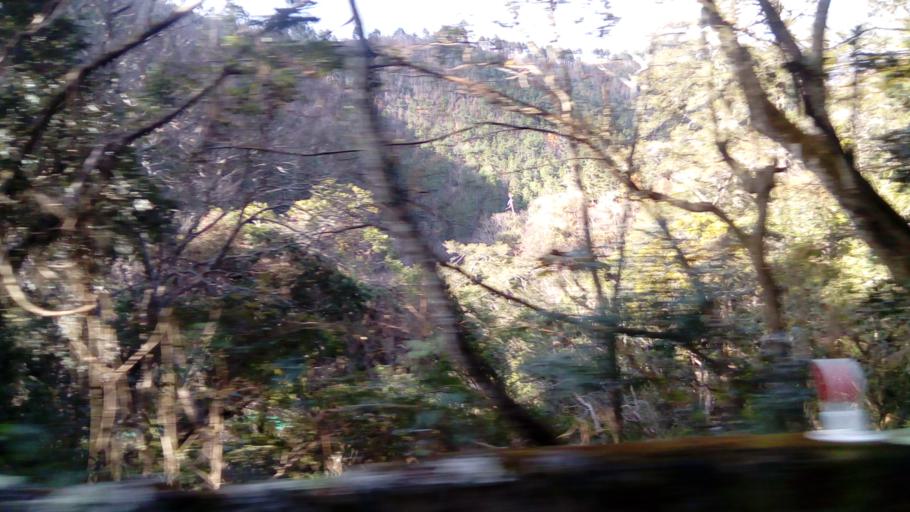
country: TW
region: Taiwan
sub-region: Hualien
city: Hualian
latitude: 24.3441
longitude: 121.3148
